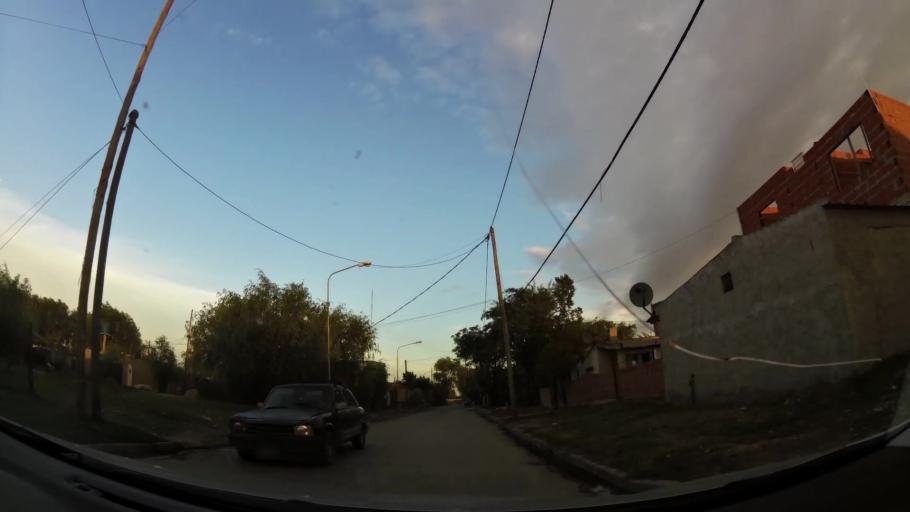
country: AR
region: Buenos Aires
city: Santa Catalina - Dique Lujan
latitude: -34.4404
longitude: -58.6621
